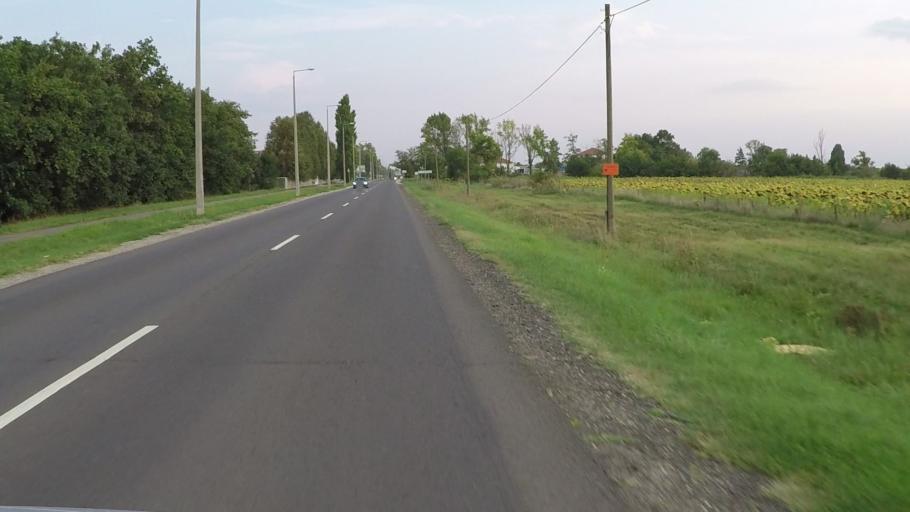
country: HU
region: Jasz-Nagykun-Szolnok
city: Szolnok
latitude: 47.1915
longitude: 20.1570
